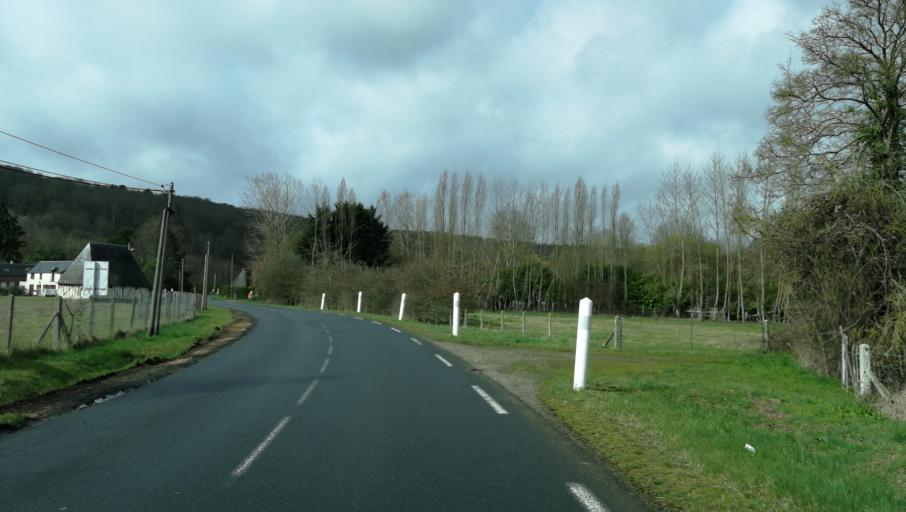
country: FR
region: Haute-Normandie
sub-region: Departement de l'Eure
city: Brionne
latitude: 49.2149
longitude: 0.7038
